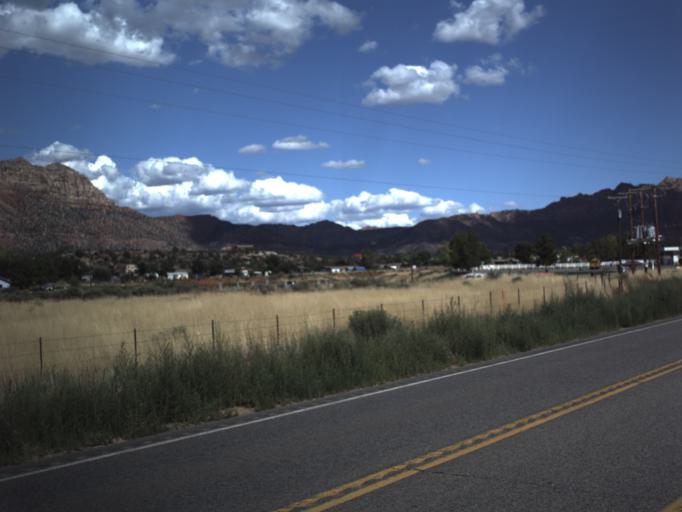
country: US
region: Utah
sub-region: Washington County
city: LaVerkin
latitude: 37.1016
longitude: -113.1312
